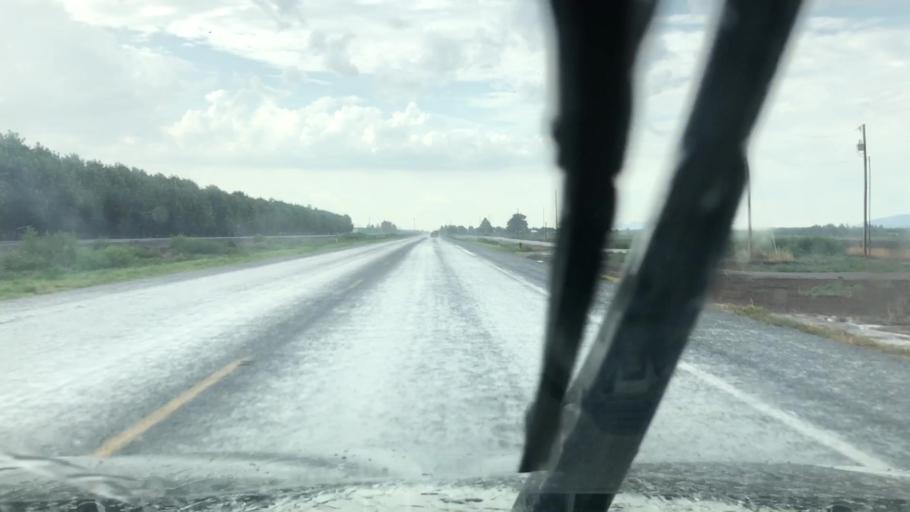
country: US
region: New Mexico
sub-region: Dona Ana County
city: Mesquite
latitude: 32.1693
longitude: -106.6996
